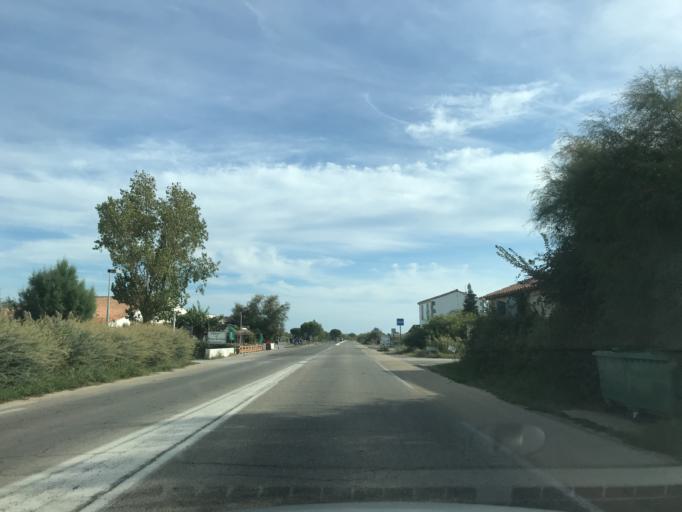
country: FR
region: Provence-Alpes-Cote d'Azur
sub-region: Departement des Bouches-du-Rhone
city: Saintes-Maries-de-la-Mer
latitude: 43.4898
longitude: 4.4036
